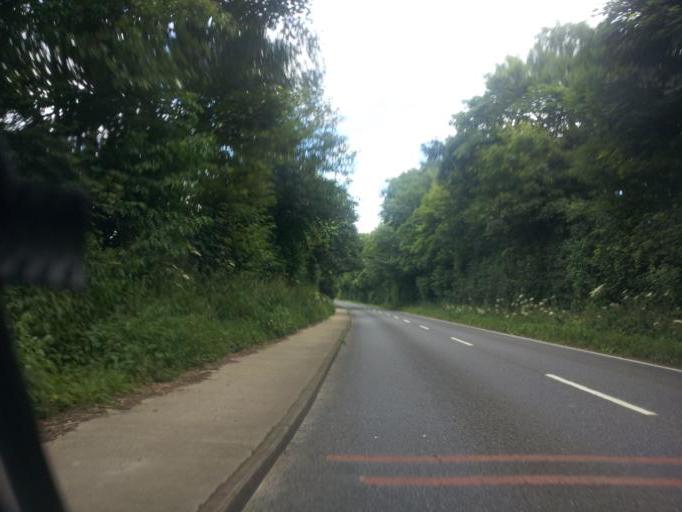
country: GB
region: England
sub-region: Kent
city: Kings Hill
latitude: 51.2580
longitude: 0.3870
